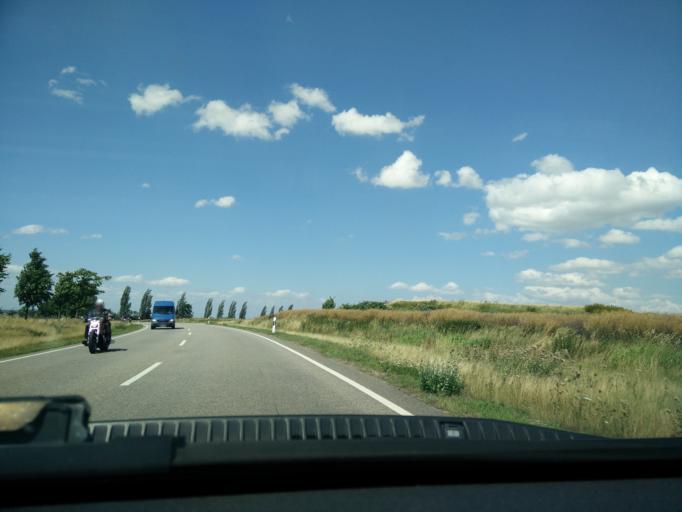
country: DE
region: Saxony
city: Muhlau
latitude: 50.9098
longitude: 12.7471
